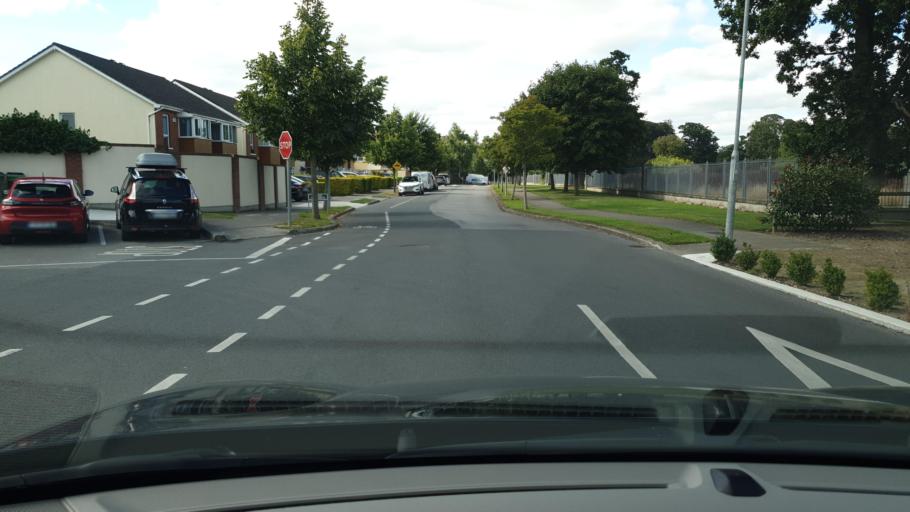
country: IE
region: Leinster
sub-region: An Mhi
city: Dunboyne
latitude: 53.4145
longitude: -6.4761
